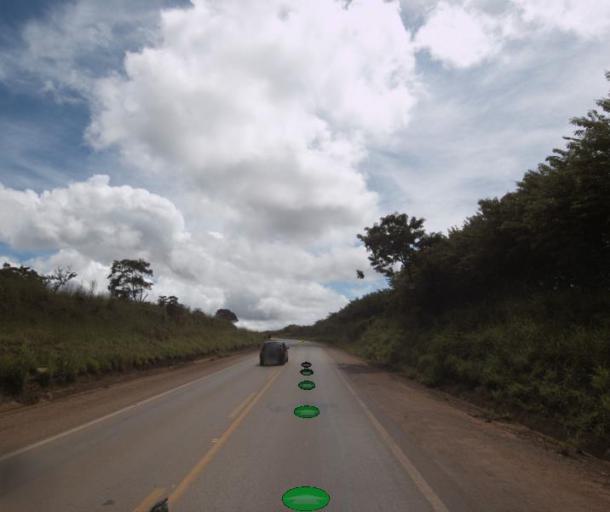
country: BR
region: Federal District
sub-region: Brasilia
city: Brasilia
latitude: -15.7466
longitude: -48.3536
